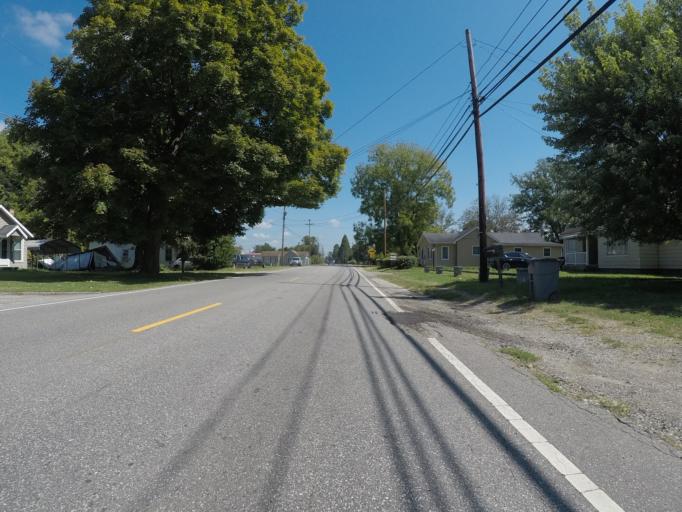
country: US
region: Ohio
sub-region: Lawrence County
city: Burlington
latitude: 38.4080
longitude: -82.5269
